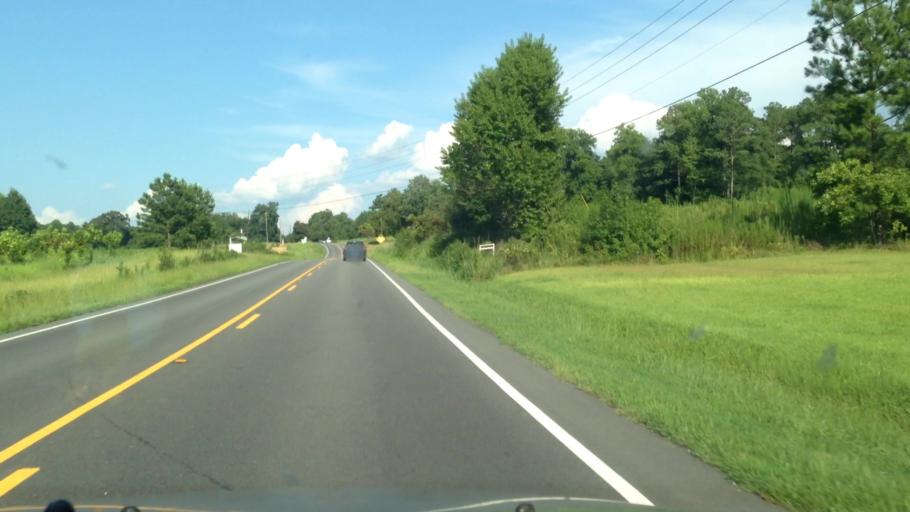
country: US
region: North Carolina
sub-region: Harnett County
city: Coats
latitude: 35.4118
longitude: -78.6856
